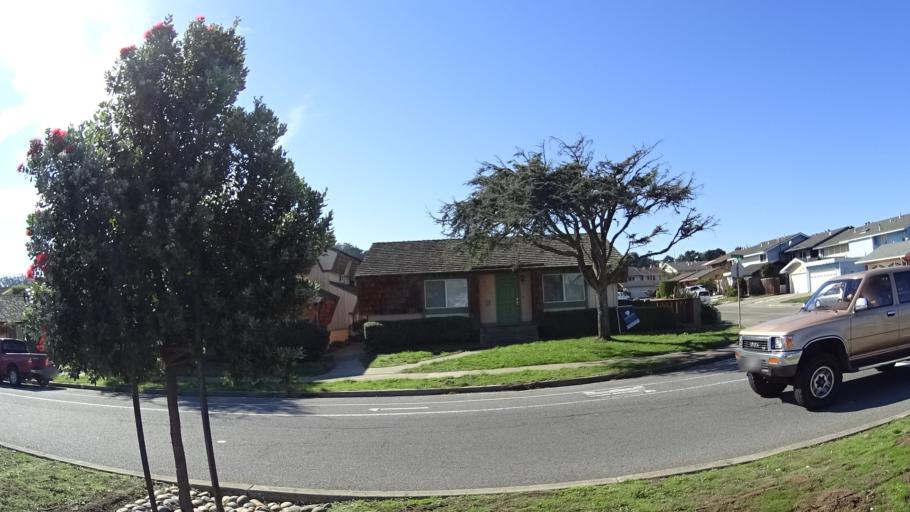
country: US
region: California
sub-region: San Mateo County
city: Colma
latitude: 37.6453
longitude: -122.4638
